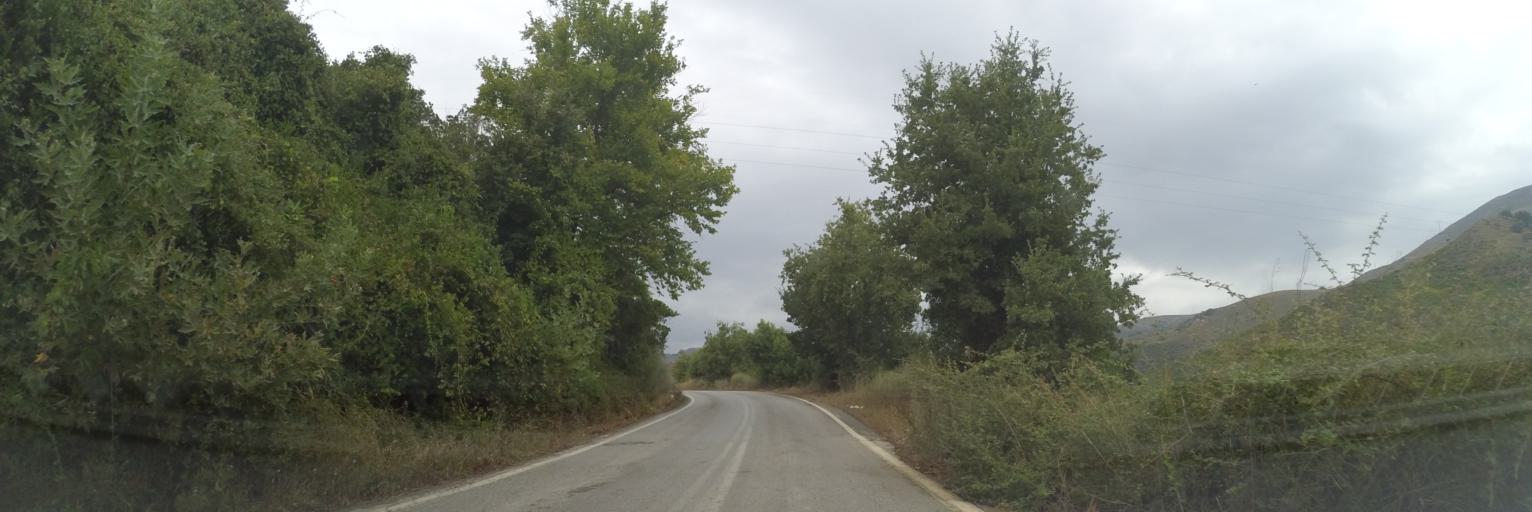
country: GR
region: Crete
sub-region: Nomos Rethymnis
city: Agia Foteini
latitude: 35.2898
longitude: 24.5628
